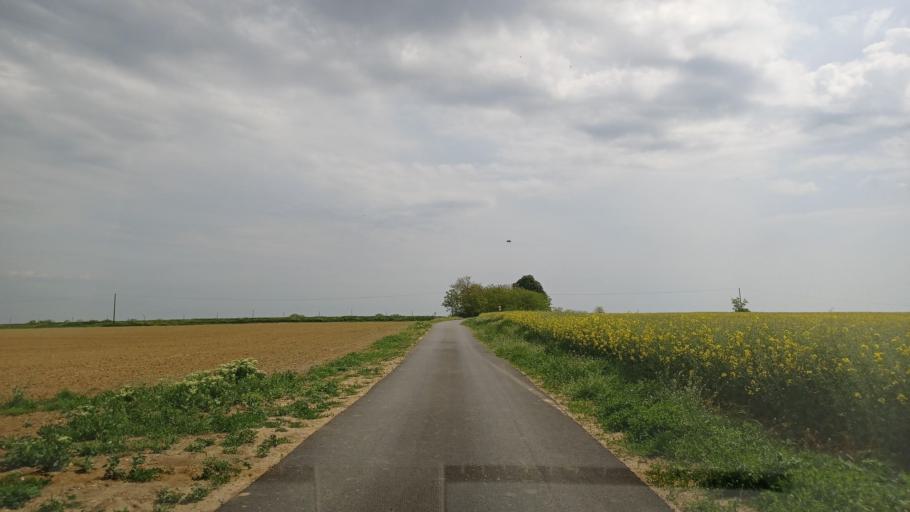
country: HU
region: Baranya
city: Kozarmisleny
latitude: 45.9705
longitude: 18.3527
